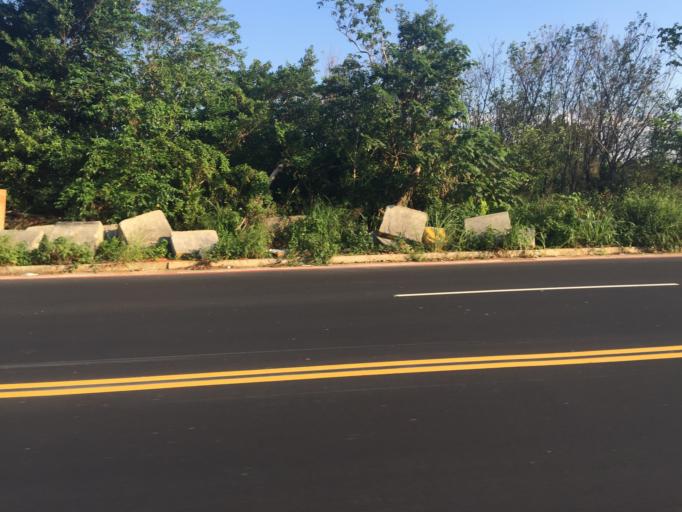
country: TW
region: Taiwan
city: Daxi
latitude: 24.9370
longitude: 121.2629
